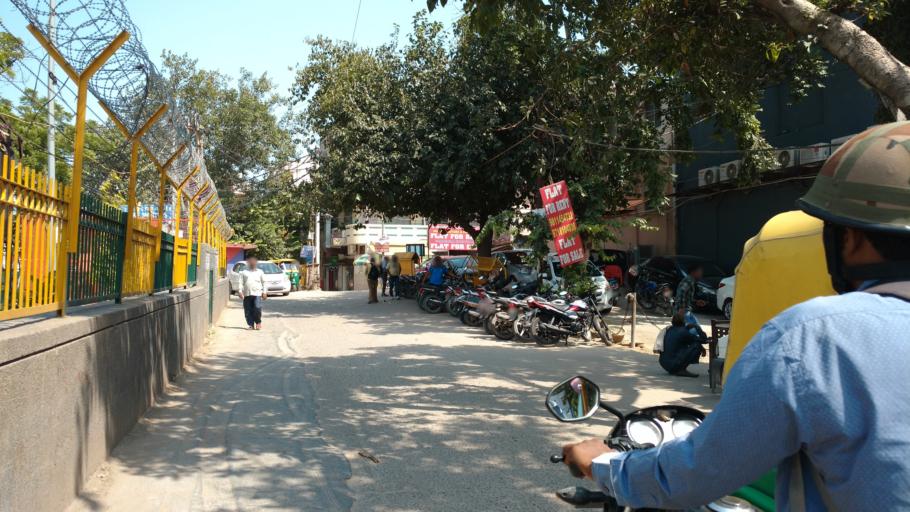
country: IN
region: NCT
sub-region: New Delhi
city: New Delhi
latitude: 28.5304
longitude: 77.2188
